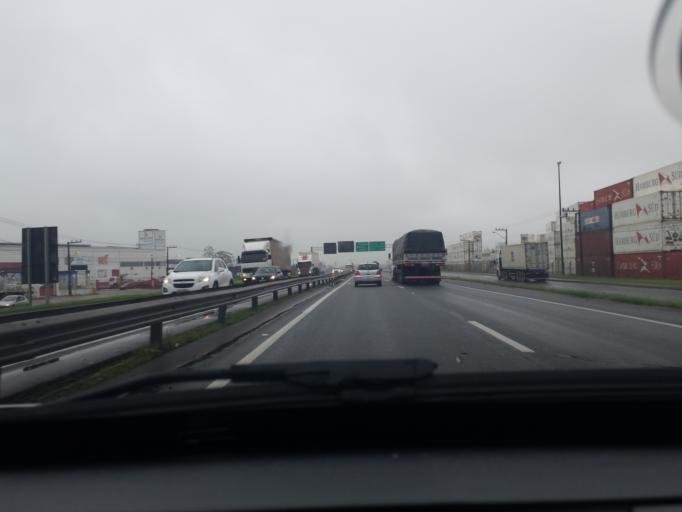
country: BR
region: Santa Catarina
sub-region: Itajai
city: Itajai
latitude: -26.8801
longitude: -48.7255
